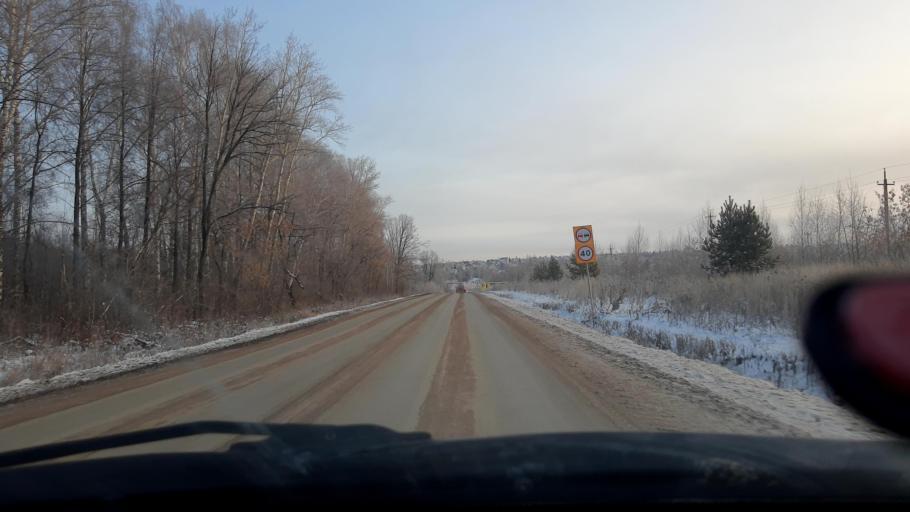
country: RU
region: Bashkortostan
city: Iglino
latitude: 54.8370
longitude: 56.4483
